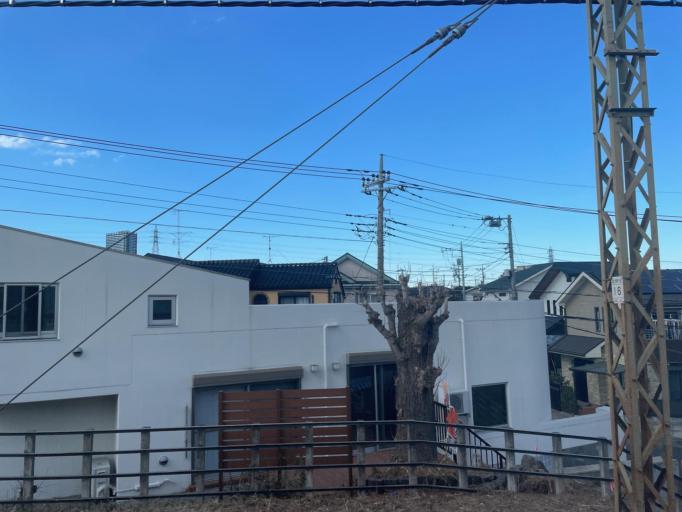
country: JP
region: Tokyo
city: Hachioji
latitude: 35.6465
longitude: 139.3460
